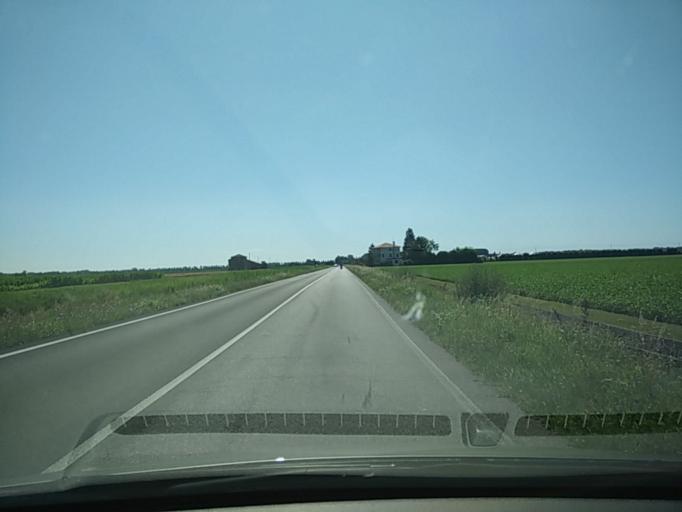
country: IT
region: Veneto
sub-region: Provincia di Venezia
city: San Giorgio di Livenza
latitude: 45.6348
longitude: 12.7670
